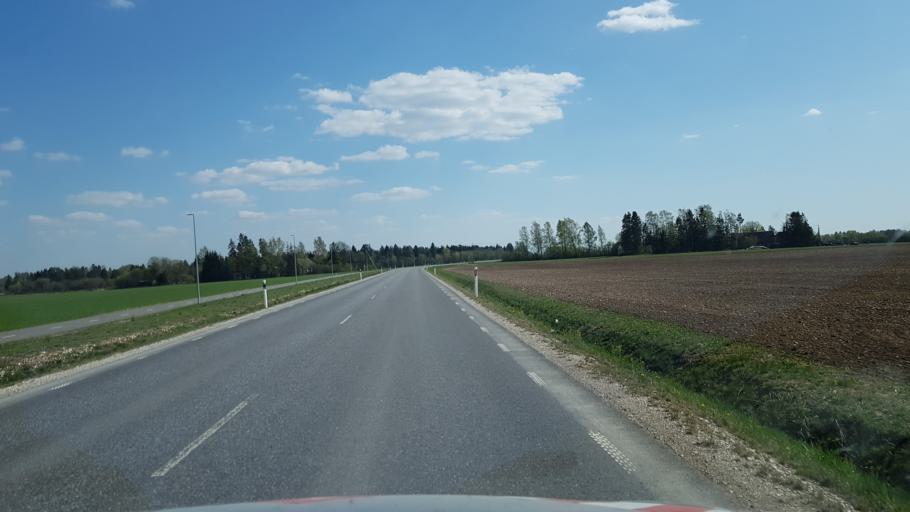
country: EE
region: Harju
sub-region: Rae vald
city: Vaida
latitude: 59.1963
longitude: 25.1072
